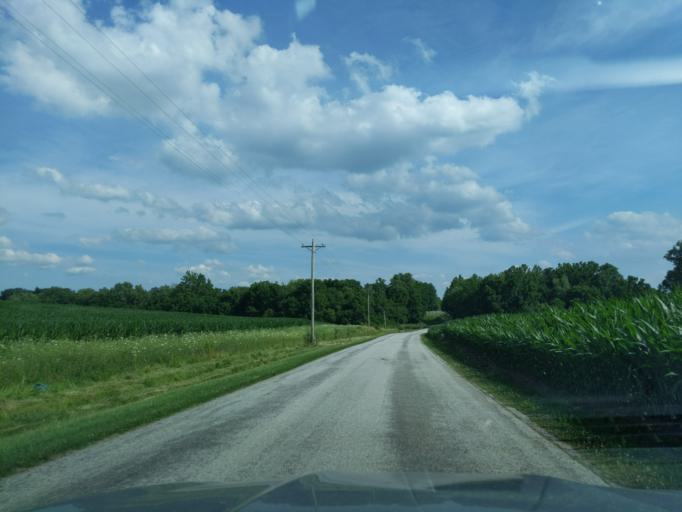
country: US
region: Indiana
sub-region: Decatur County
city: Greensburg
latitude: 39.2901
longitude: -85.4681
